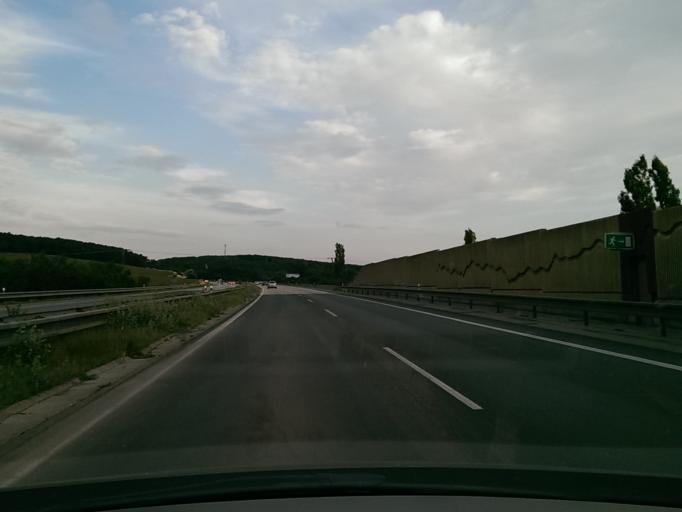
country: CZ
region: South Moravian
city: Ricany
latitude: 49.2028
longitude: 16.4212
